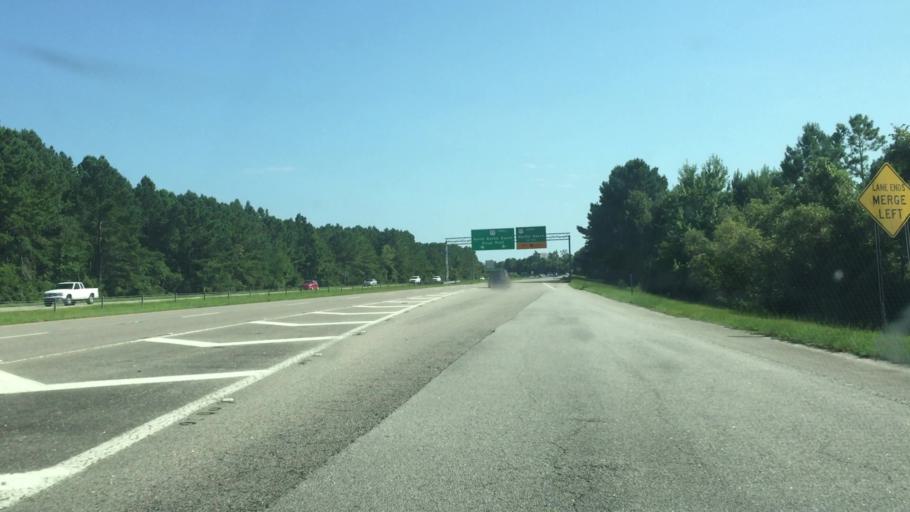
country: US
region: South Carolina
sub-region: Horry County
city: North Myrtle Beach
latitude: 33.8040
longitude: -78.7792
